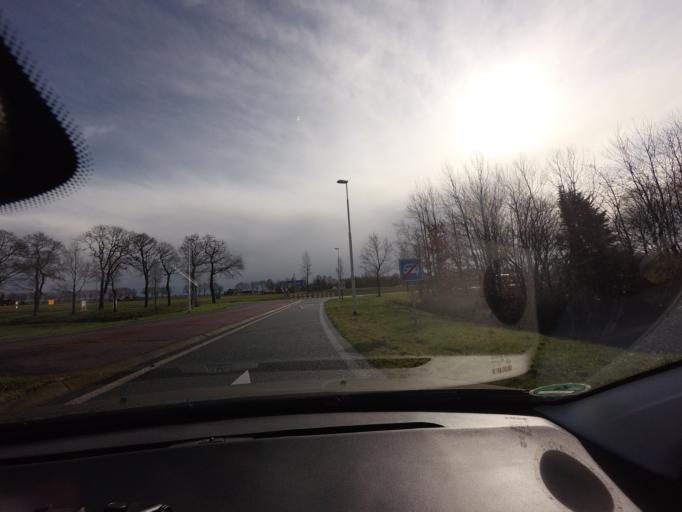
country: NL
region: Groningen
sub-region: Gemeente Veendam
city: Veendam
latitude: 53.0416
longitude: 6.8262
